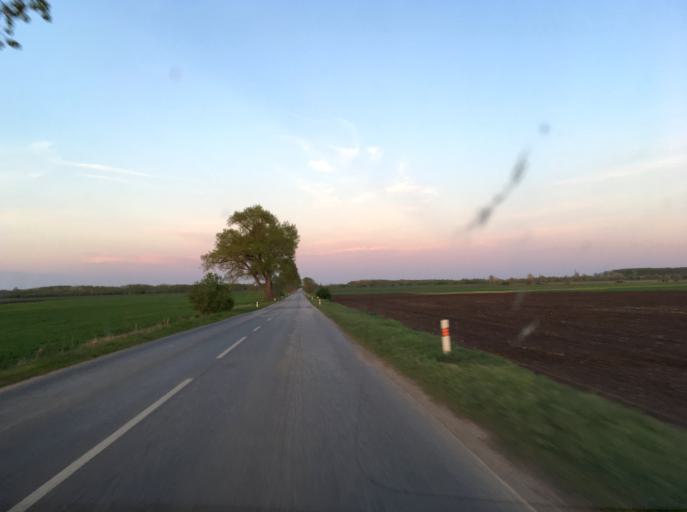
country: SK
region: Nitriansky
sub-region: Okres Nove Zamky
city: Nove Zamky
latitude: 47.9222
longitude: 18.0915
